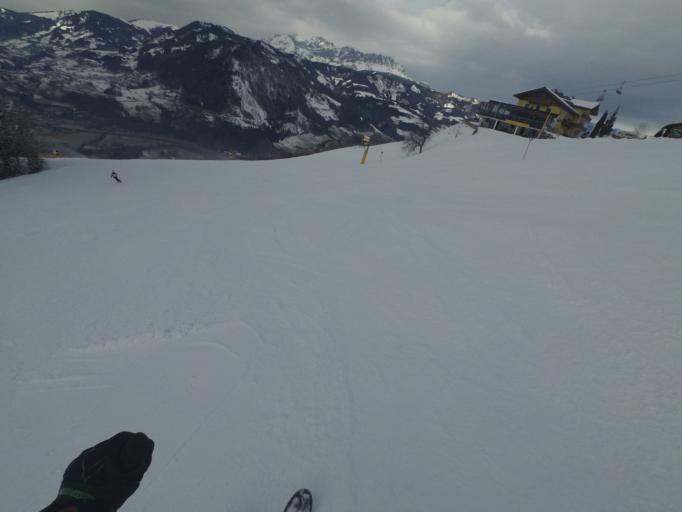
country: AT
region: Salzburg
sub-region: Politischer Bezirk Sankt Johann im Pongau
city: Sankt Johann im Pongau
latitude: 47.3195
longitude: 13.2050
